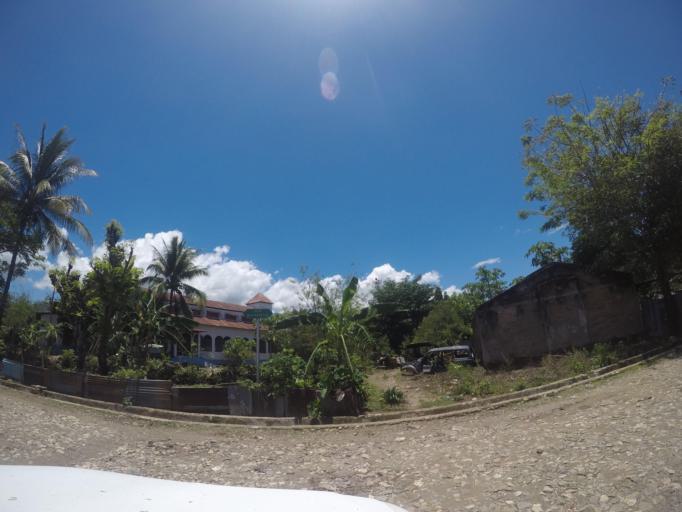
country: TL
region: Bobonaro
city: Maliana
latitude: -8.9886
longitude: 125.2154
